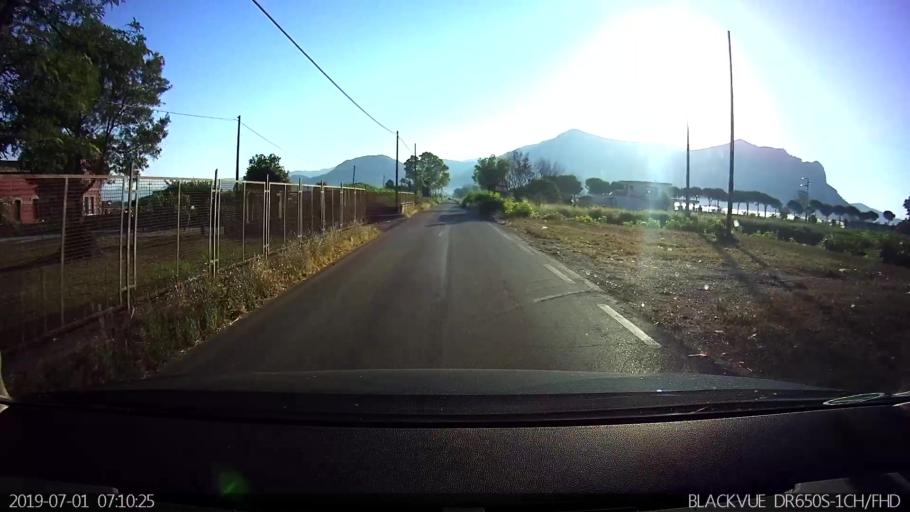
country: IT
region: Latium
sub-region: Provincia di Latina
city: Borgo Hermada
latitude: 41.3120
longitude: 13.1701
